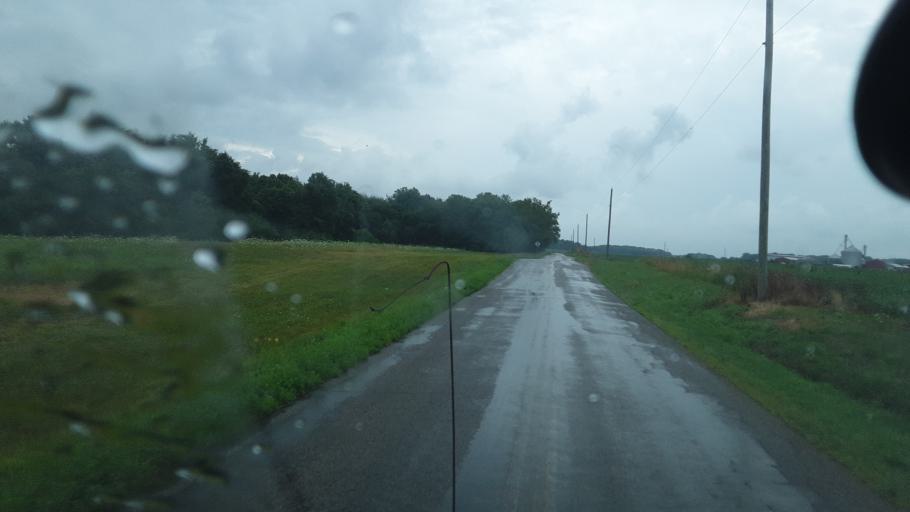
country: US
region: Ohio
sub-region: Williams County
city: Edgerton
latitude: 41.5250
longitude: -84.7948
